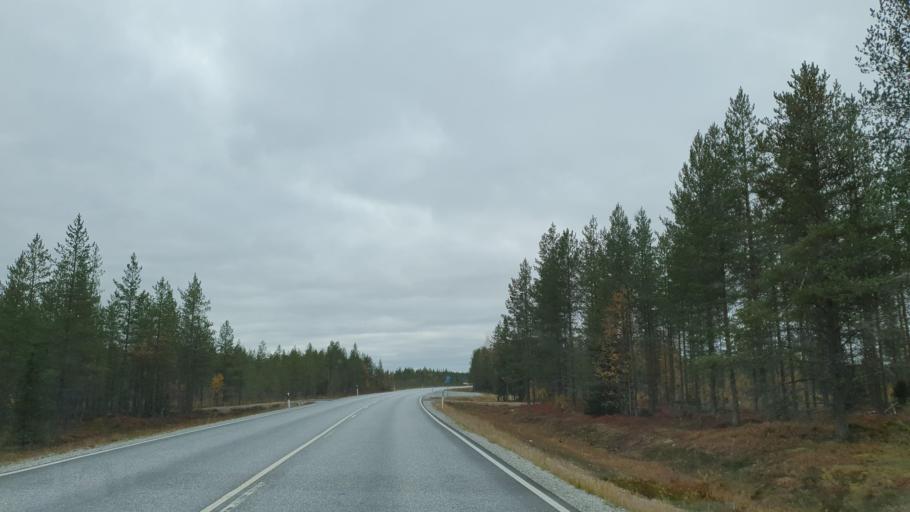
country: FI
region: Northern Ostrobothnia
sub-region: Oulunkaari
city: Pudasjaervi
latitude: 65.6020
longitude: 26.7238
